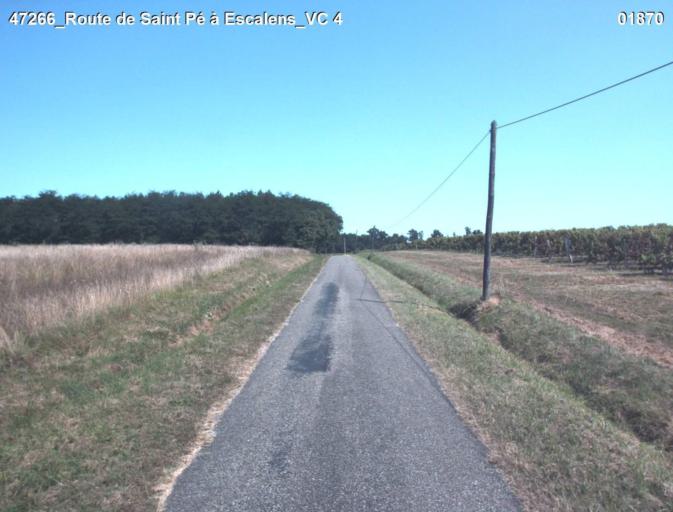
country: FR
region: Aquitaine
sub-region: Departement des Landes
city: Gabarret
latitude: 43.9999
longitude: 0.0829
